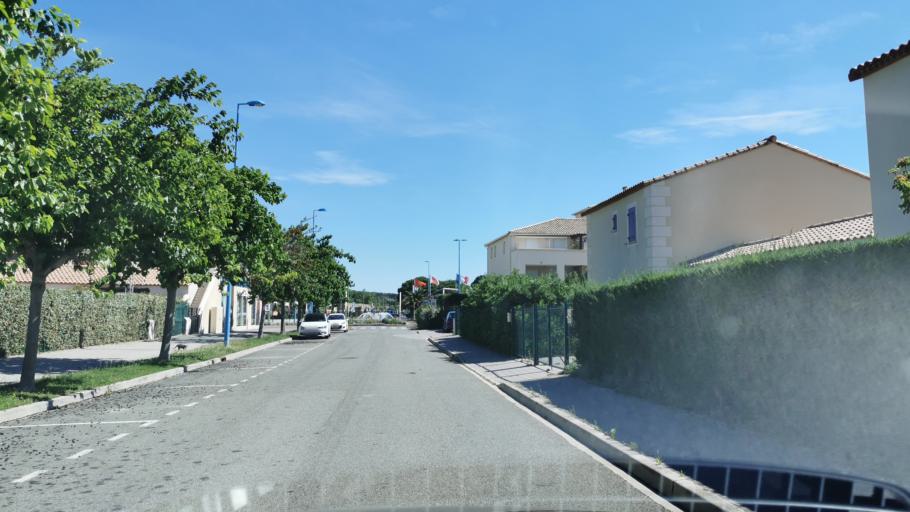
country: FR
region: Languedoc-Roussillon
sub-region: Departement de l'Aude
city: Armissan
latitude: 43.1589
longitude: 3.1623
